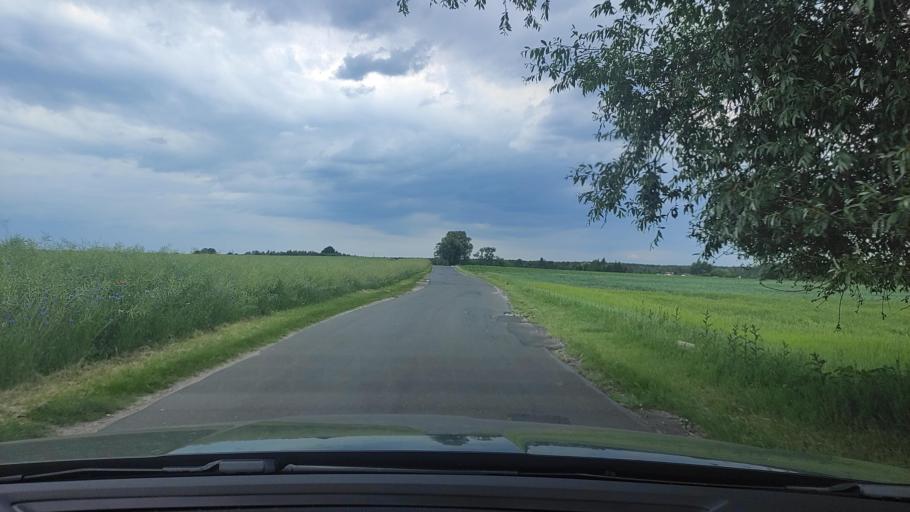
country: PL
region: Greater Poland Voivodeship
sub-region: Powiat poznanski
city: Kostrzyn
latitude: 52.4883
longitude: 17.1904
